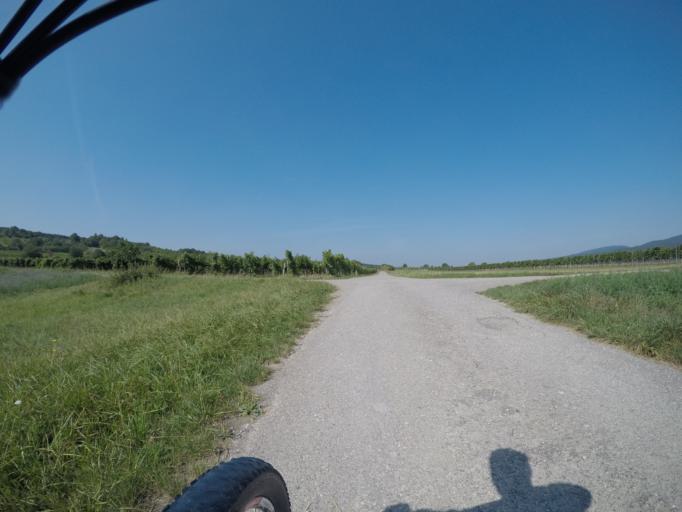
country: AT
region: Lower Austria
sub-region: Politischer Bezirk Baden
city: Hirtenberg
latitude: 47.9503
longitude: 16.1798
